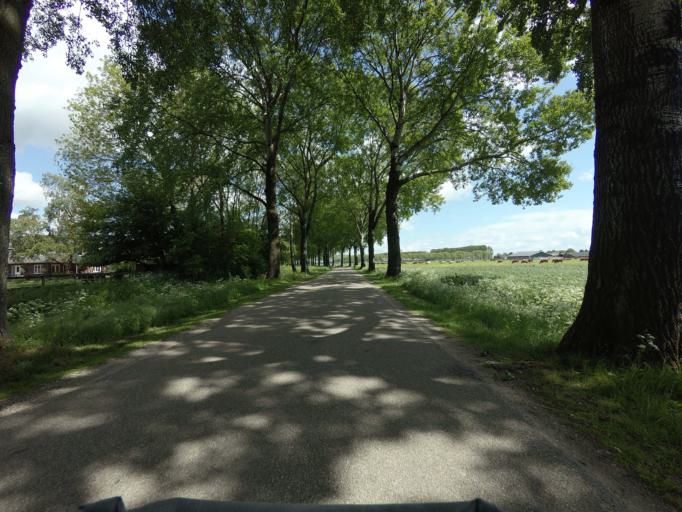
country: NL
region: North Brabant
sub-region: Gemeente Woudrichem
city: Woudrichem
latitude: 51.8454
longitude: 5.0469
